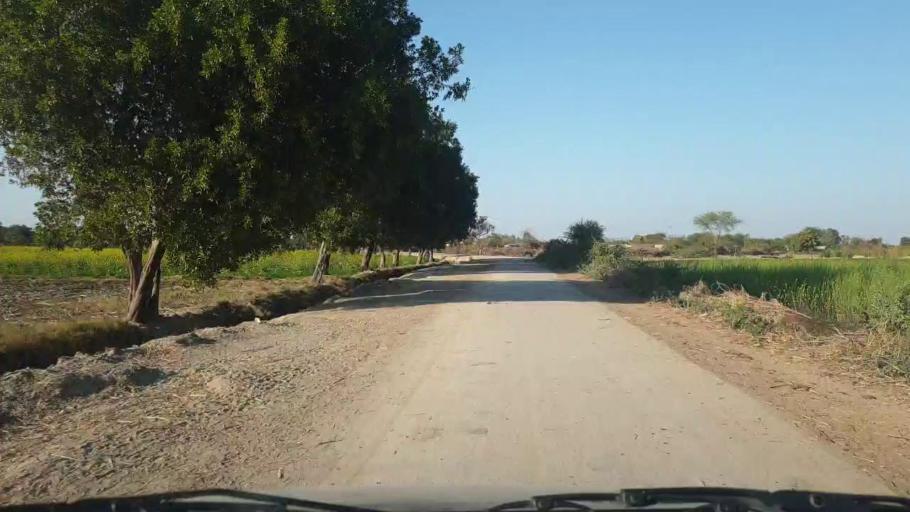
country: PK
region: Sindh
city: Samaro
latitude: 25.3544
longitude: 69.2865
